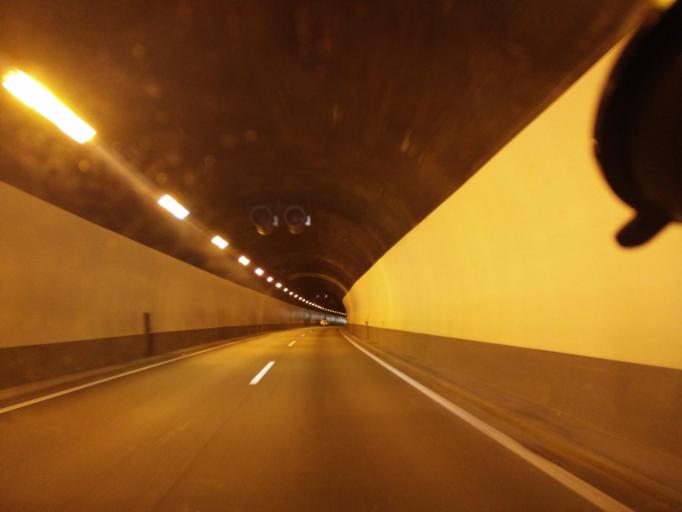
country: ES
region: Catalonia
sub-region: Provincia de Barcelona
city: Sant Cugat del Valles
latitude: 41.4417
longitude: 2.0705
